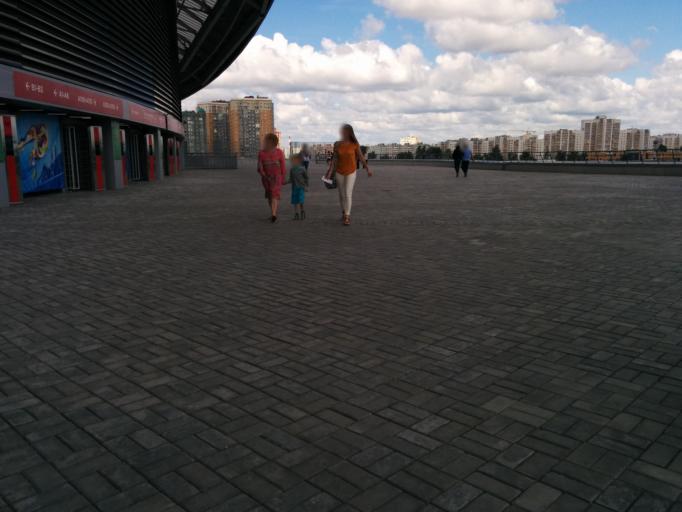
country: RU
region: Tatarstan
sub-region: Gorod Kazan'
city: Kazan
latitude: 55.8216
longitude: 49.1627
